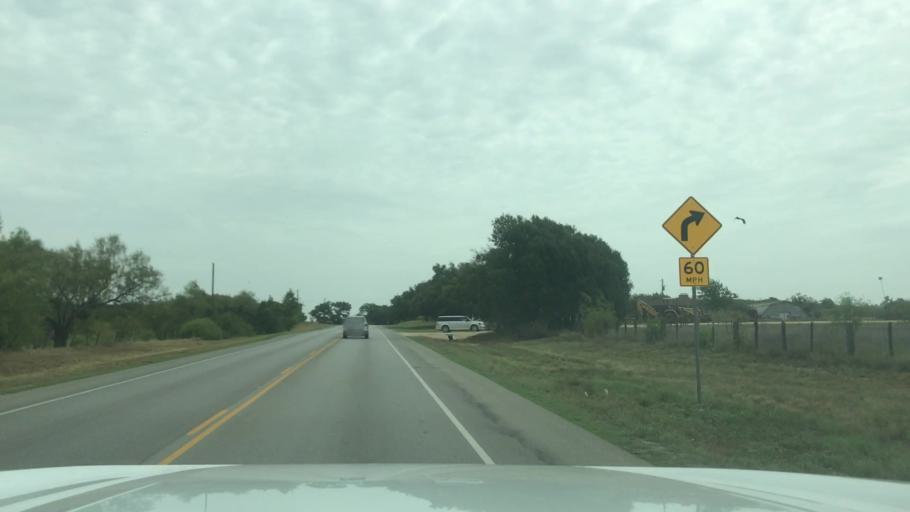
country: US
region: Texas
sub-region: Erath County
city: Dublin
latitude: 32.0976
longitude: -98.4016
